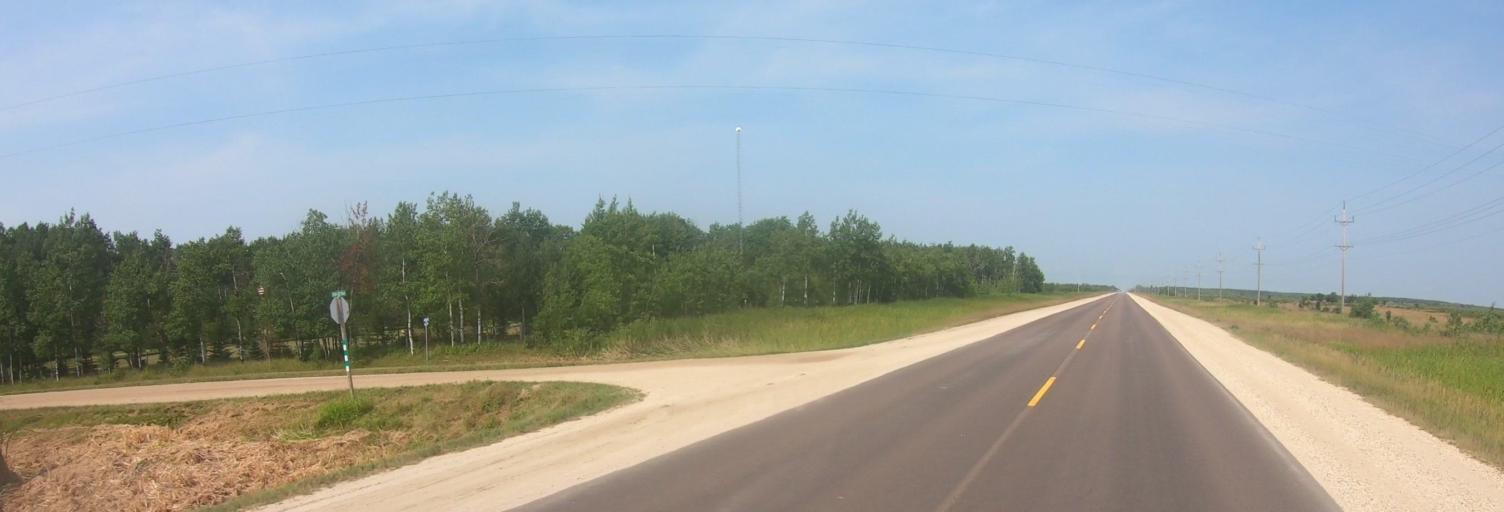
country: CA
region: Manitoba
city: La Broquerie
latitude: 49.2728
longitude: -96.4870
